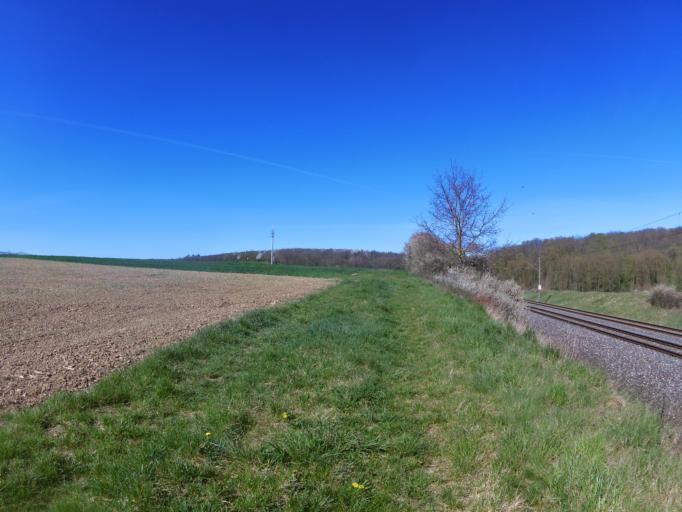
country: DE
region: Bavaria
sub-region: Regierungsbezirk Unterfranken
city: Rottendorf
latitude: 49.8124
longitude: 10.0603
